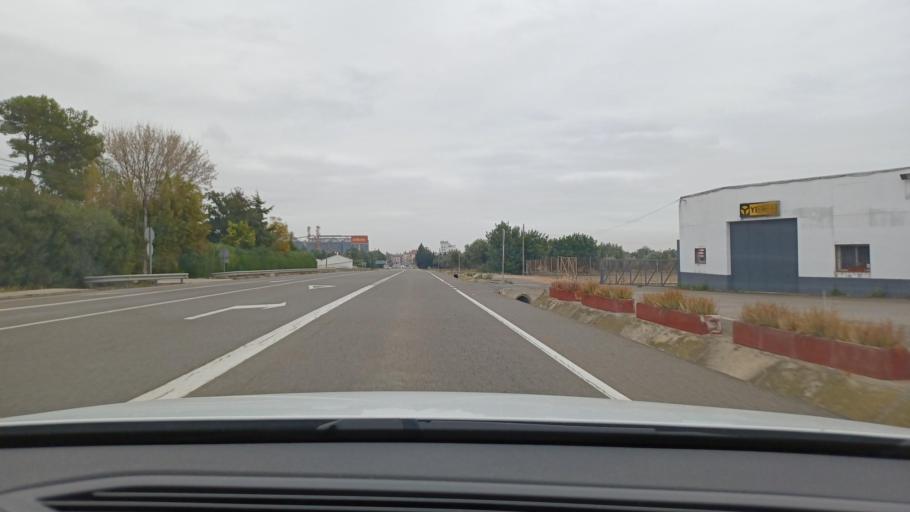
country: ES
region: Catalonia
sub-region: Provincia de Tarragona
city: Amposta
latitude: 40.7504
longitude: 0.6144
